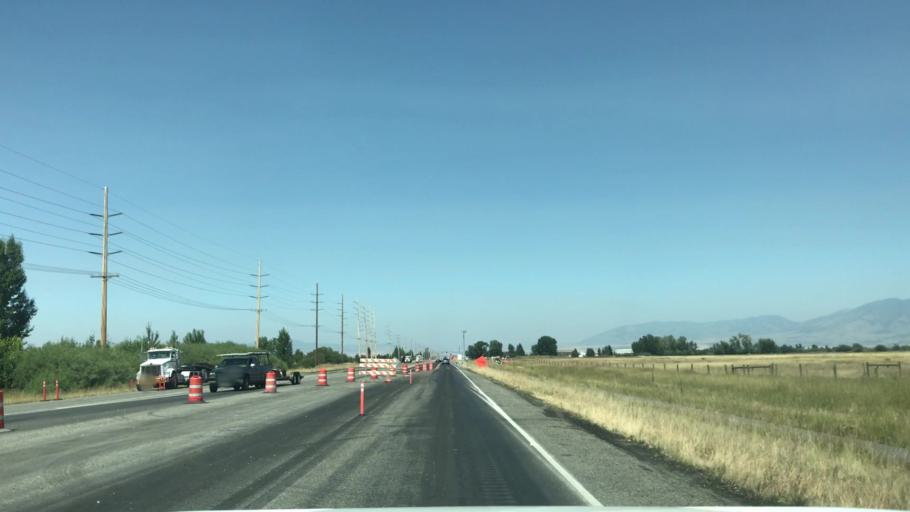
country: US
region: Montana
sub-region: Gallatin County
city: Belgrade
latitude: 45.7155
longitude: -111.1851
